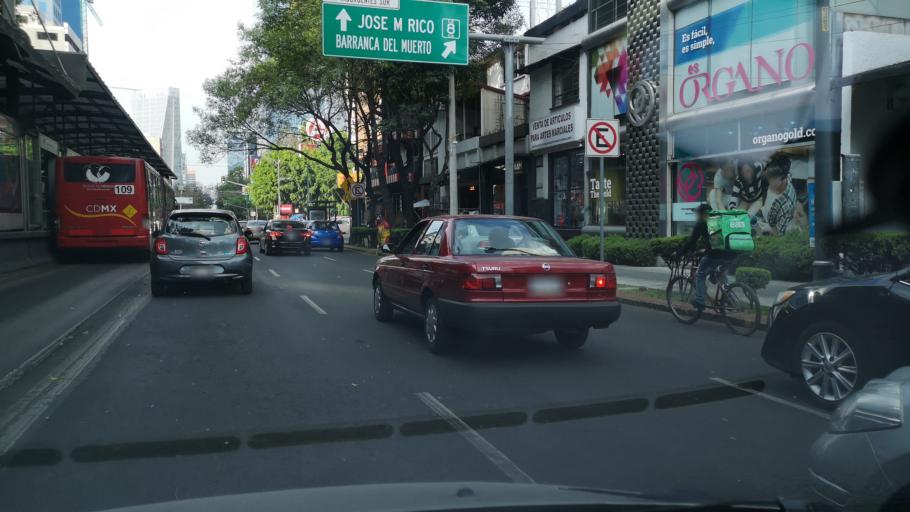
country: MX
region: Mexico City
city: Alvaro Obregon
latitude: 19.3613
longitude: -99.1829
